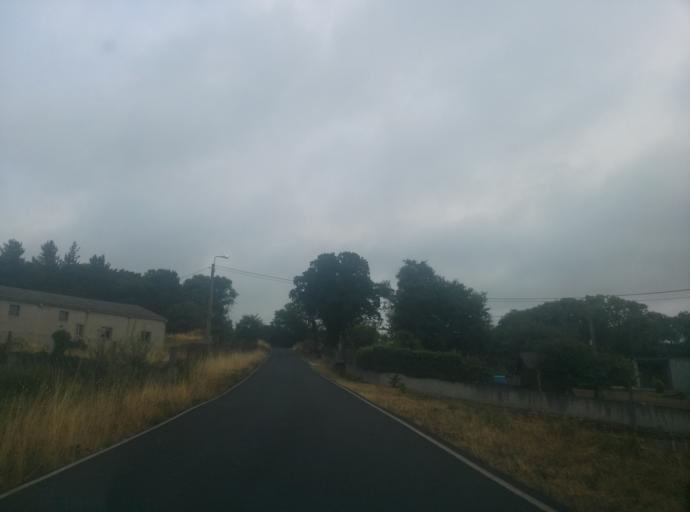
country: ES
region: Galicia
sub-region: Provincia de Lugo
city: Outeiro de Rei
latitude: 43.0826
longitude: -7.5473
